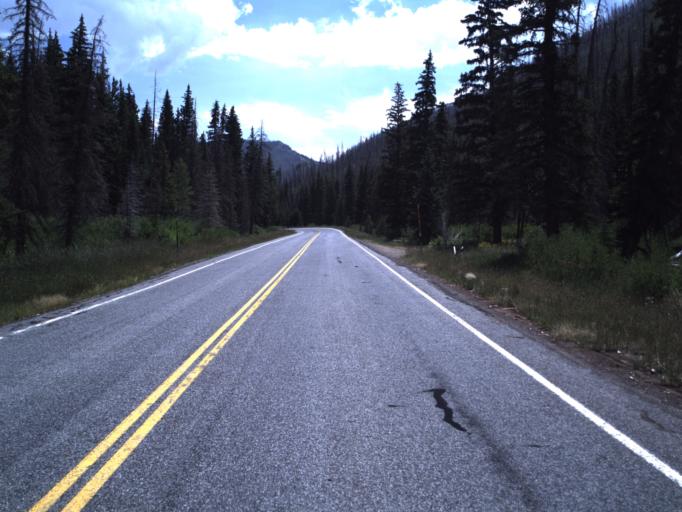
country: US
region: Utah
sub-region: Sanpete County
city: Fairview
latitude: 39.5534
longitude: -111.1707
